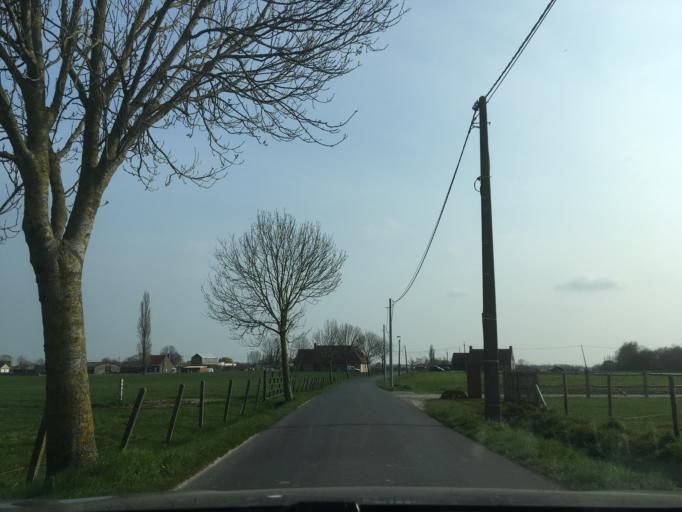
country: BE
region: Flanders
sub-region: Provincie West-Vlaanderen
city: Izegem
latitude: 50.9470
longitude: 3.2181
